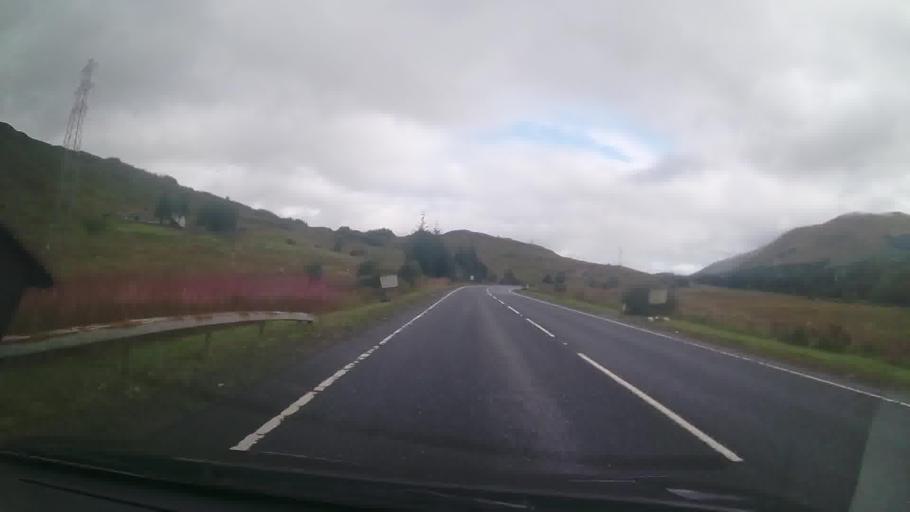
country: GB
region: Scotland
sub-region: Argyll and Bute
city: Garelochhead
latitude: 56.3803
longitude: -4.6418
